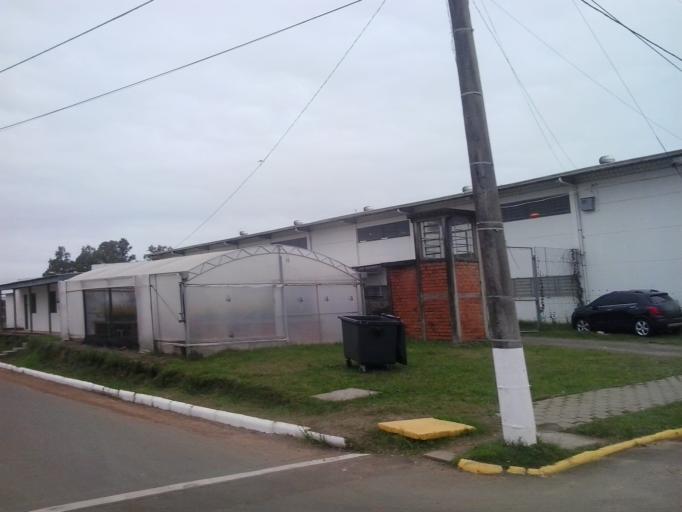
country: BR
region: Rio Grande do Sul
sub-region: Santa Maria
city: Santa Maria
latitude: -29.7143
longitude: -53.7189
